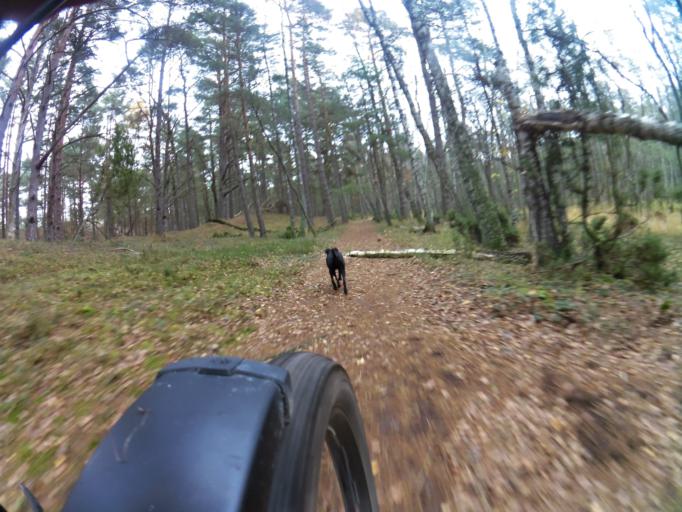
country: PL
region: Pomeranian Voivodeship
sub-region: Powiat leborski
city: Leba
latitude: 54.7757
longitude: 17.6718
